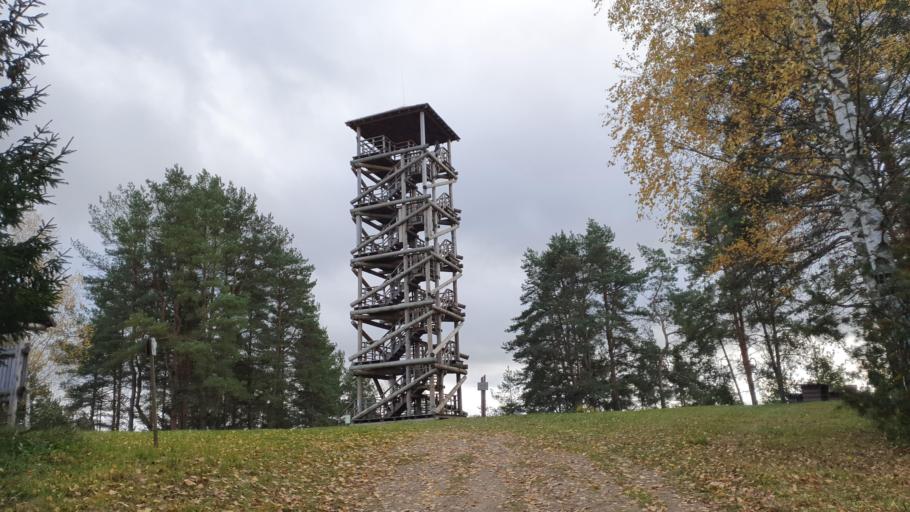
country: LV
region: Daugavpils
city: Daugavpils
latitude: 55.9152
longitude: 26.8151
